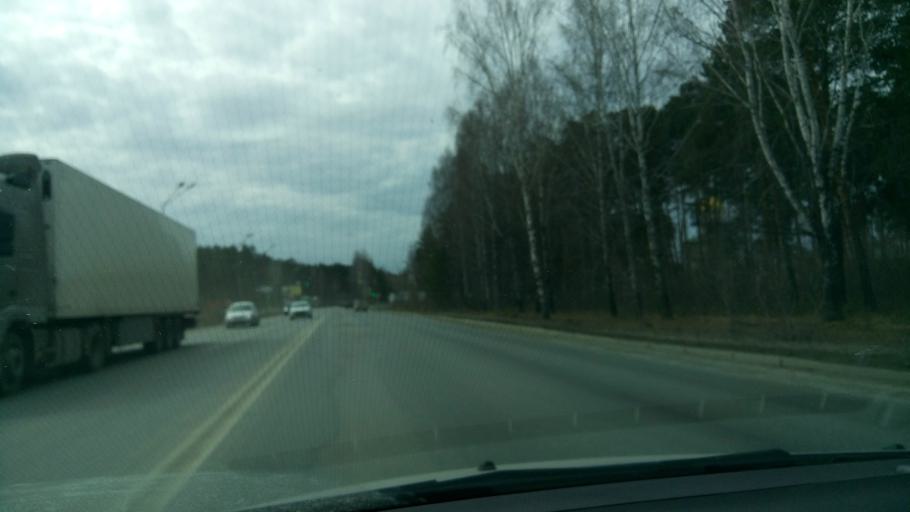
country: RU
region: Sverdlovsk
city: Beryozovsky
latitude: 56.8923
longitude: 60.7470
